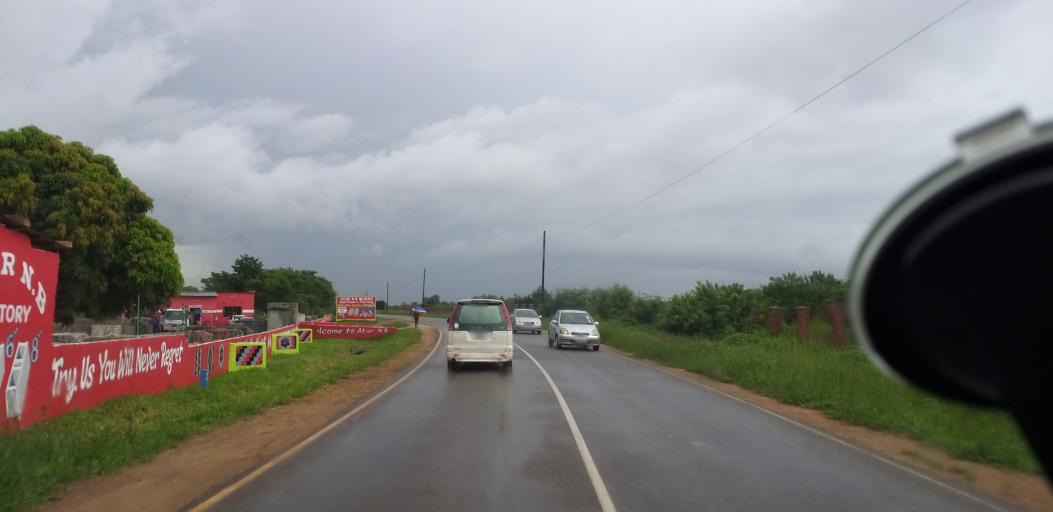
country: ZM
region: Lusaka
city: Lusaka
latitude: -15.4882
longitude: 28.3146
